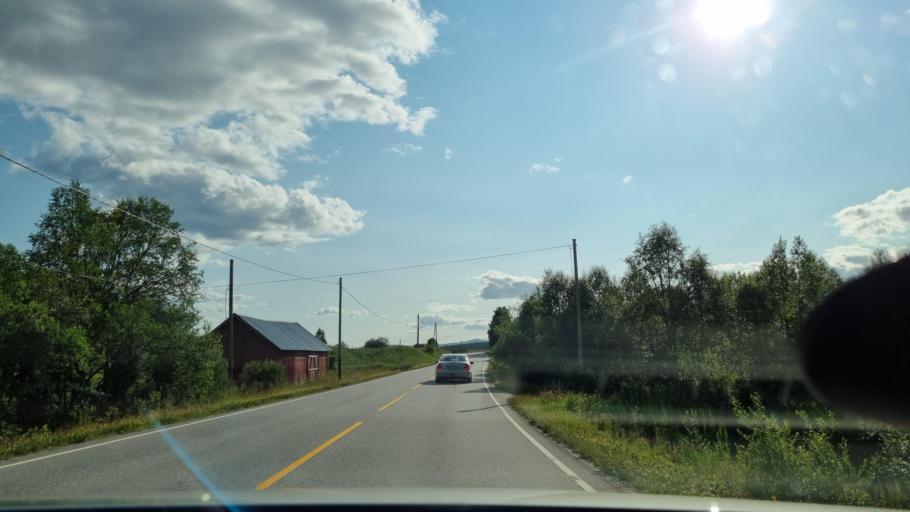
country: NO
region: Hedmark
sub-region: Os
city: Os
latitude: 62.5176
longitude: 11.2911
